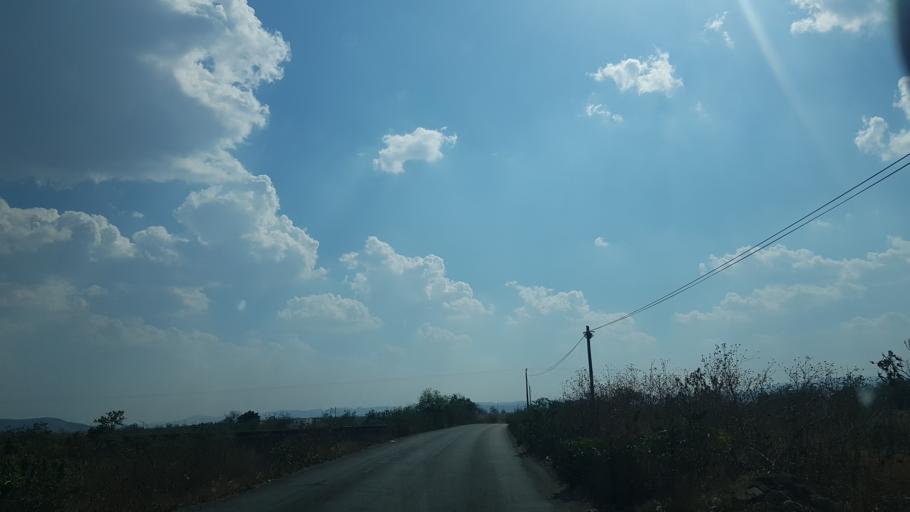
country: MX
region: Puebla
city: Atlixco
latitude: 18.9031
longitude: -98.4856
